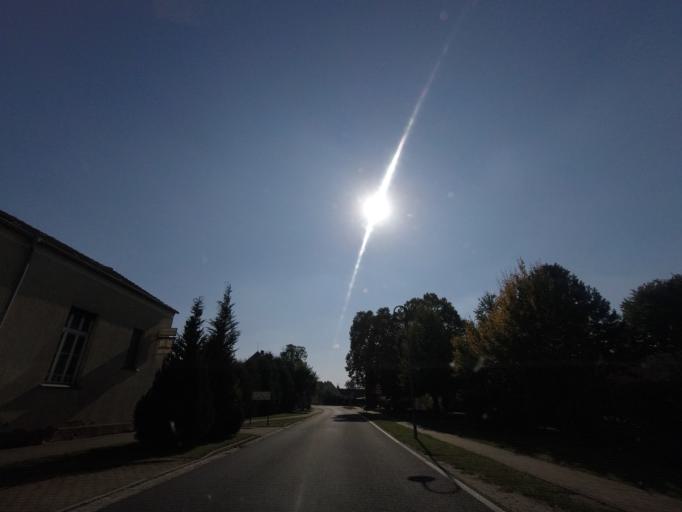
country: DE
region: Brandenburg
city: Niedergorsdorf
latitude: 51.9540
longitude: 12.9793
